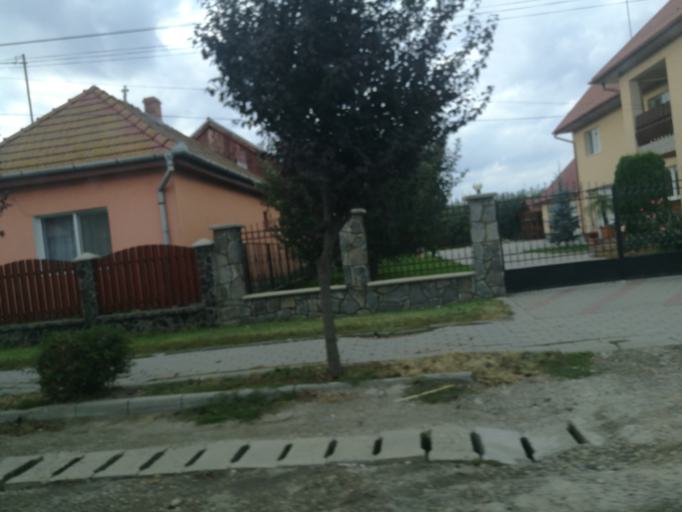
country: RO
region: Mures
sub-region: Comuna Ungheni
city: Ungheni
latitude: 46.4868
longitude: 24.4611
